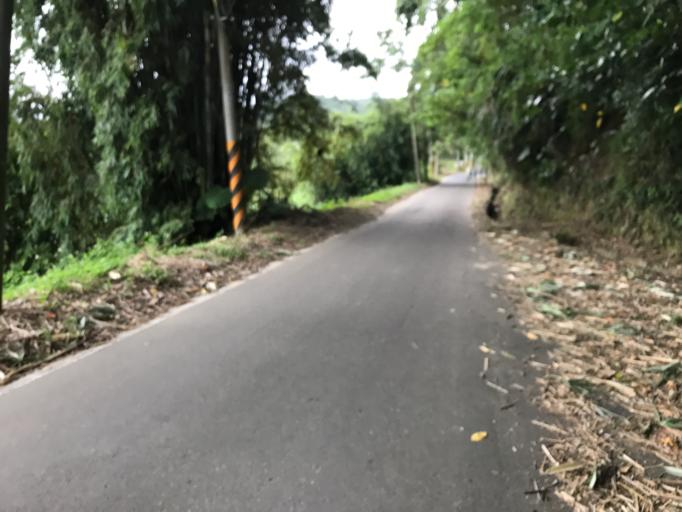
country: TW
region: Taiwan
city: Daxi
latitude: 24.7789
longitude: 121.1739
